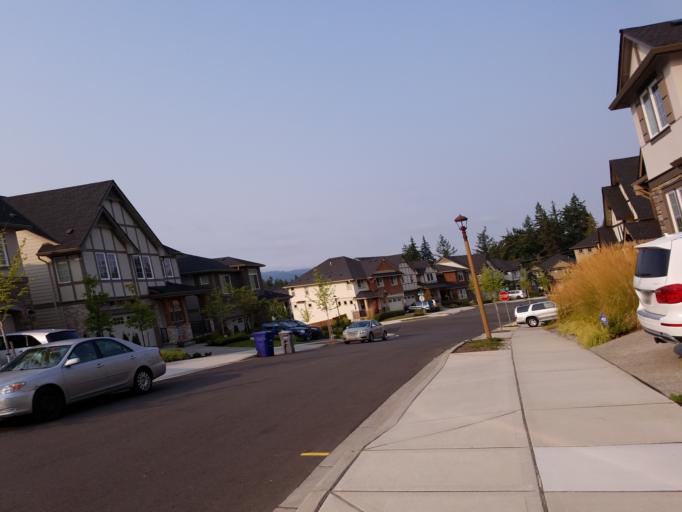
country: US
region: Washington
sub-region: King County
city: City of Sammamish
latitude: 47.5933
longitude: -122.0329
